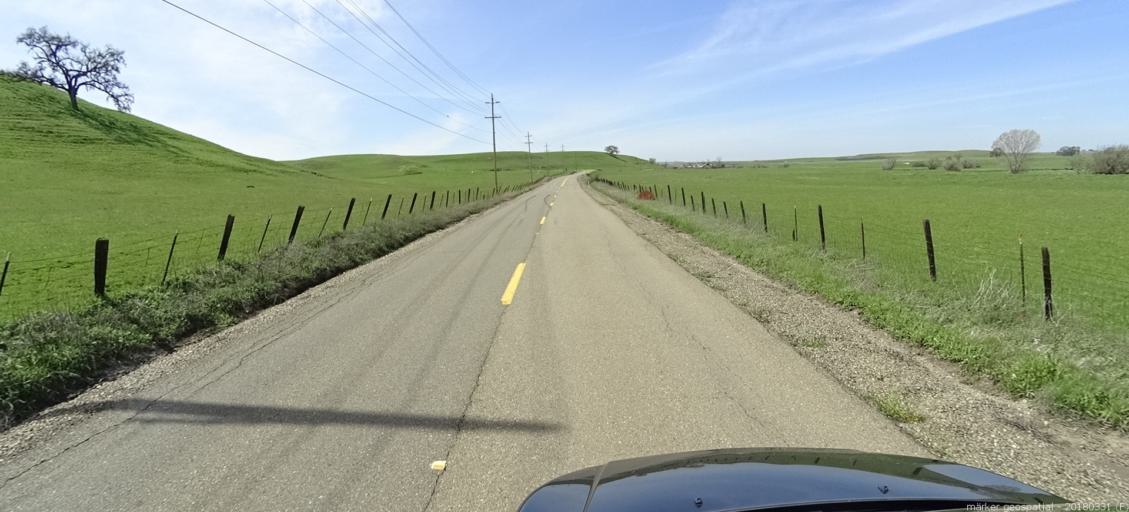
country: US
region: California
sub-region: Sacramento County
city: Rancho Murieta
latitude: 38.5173
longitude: -121.1082
